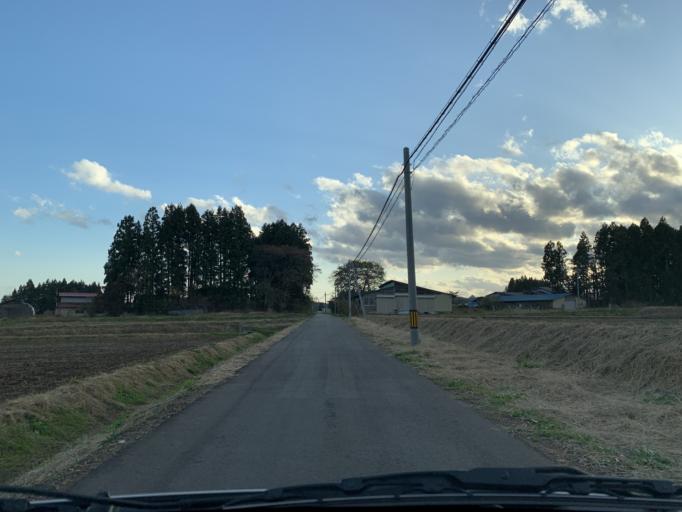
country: JP
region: Iwate
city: Mizusawa
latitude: 39.0912
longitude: 141.0374
